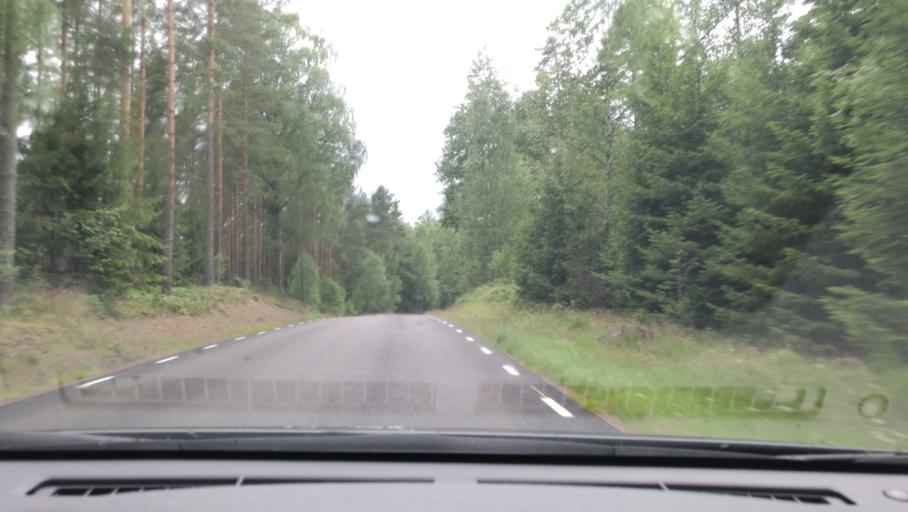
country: SE
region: OEstergoetland
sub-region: Norrkopings Kommun
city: Jursla
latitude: 58.8060
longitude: 16.1181
